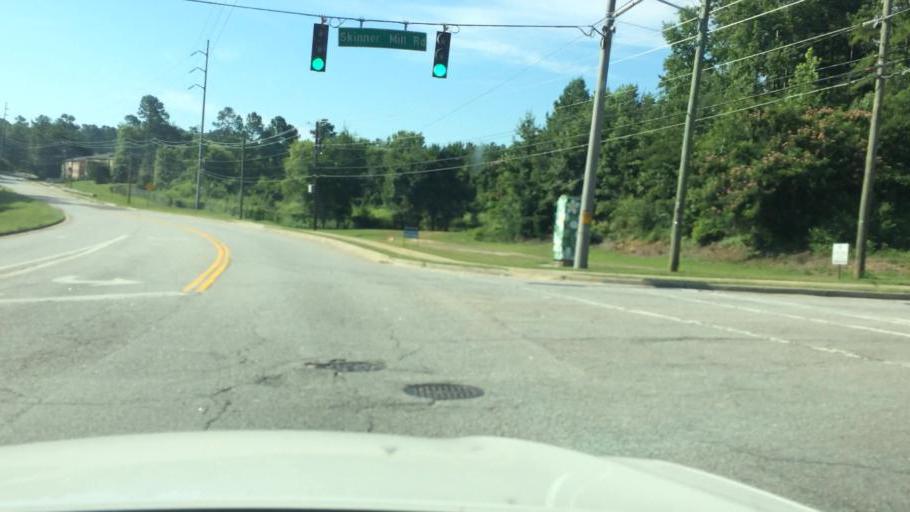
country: US
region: Georgia
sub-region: Columbia County
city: Martinez
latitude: 33.5058
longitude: -82.0424
